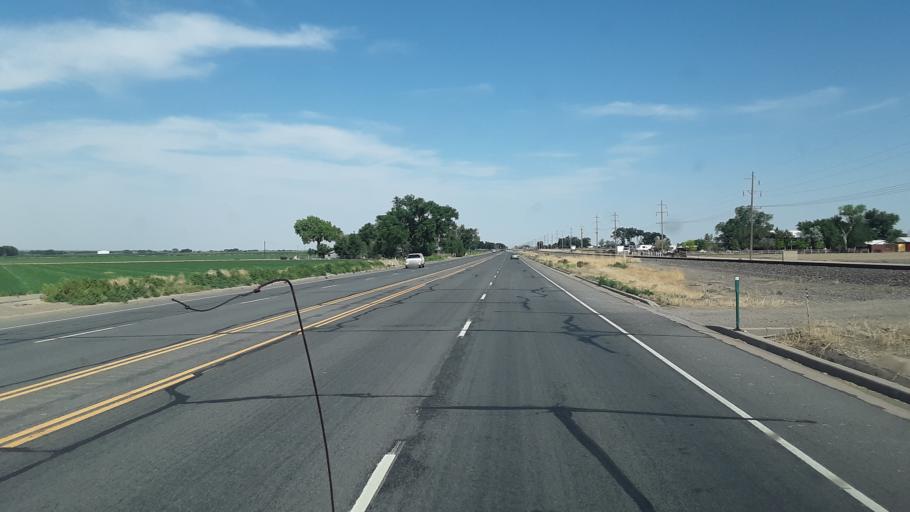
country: US
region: Colorado
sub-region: Otero County
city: Rocky Ford
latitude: 38.0991
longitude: -103.8342
